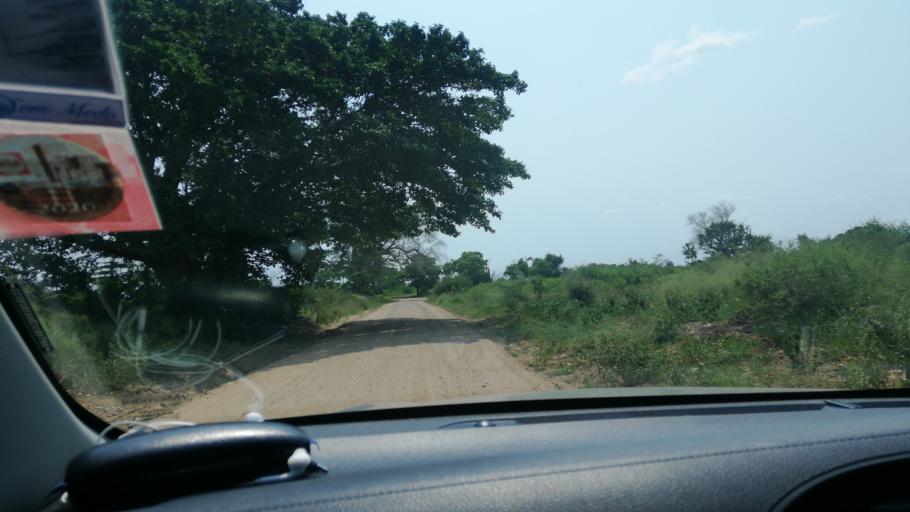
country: MZ
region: Maputo
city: Matola
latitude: -26.0582
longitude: 32.3888
